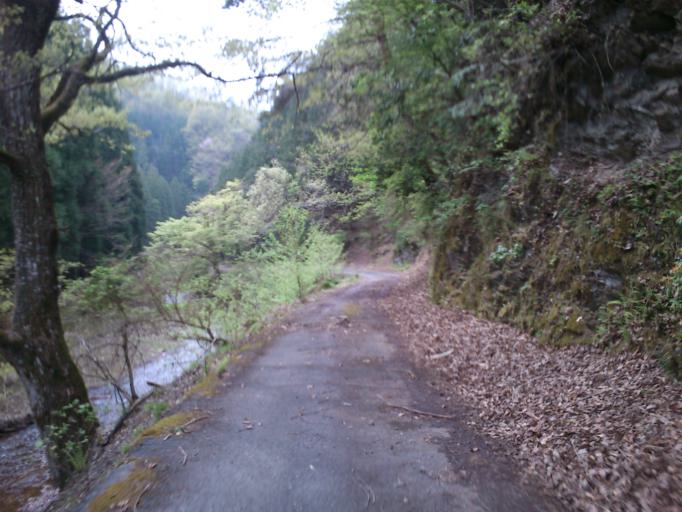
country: JP
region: Kyoto
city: Maizuru
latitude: 35.3987
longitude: 135.5010
